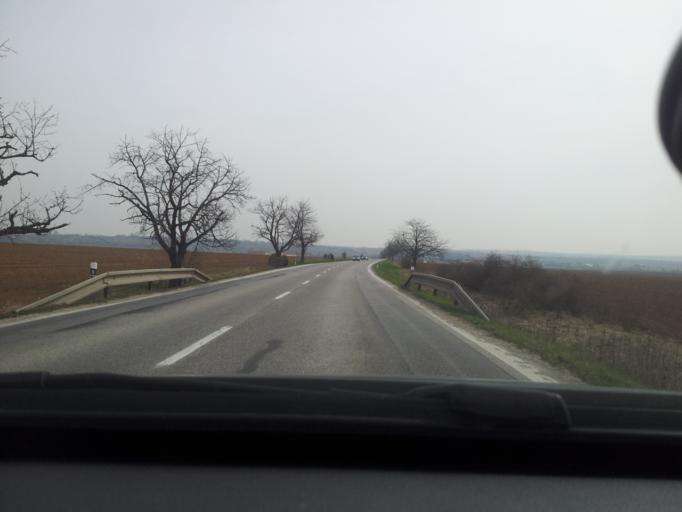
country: SK
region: Nitriansky
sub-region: Okres Nitra
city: Nitra
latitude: 48.3022
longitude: 18.1590
